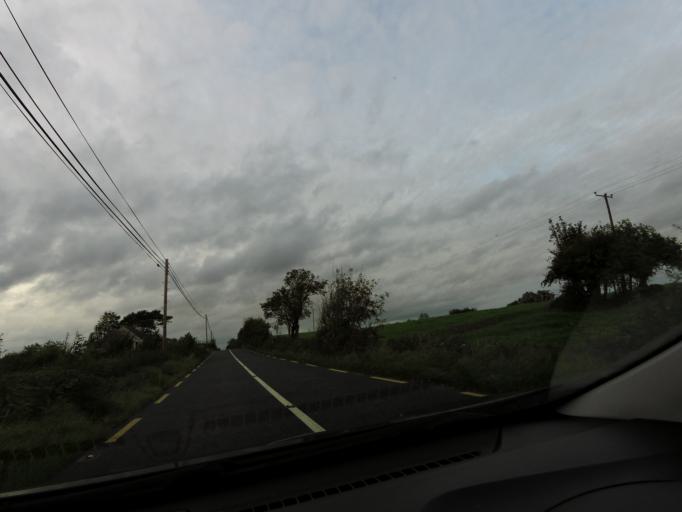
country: IE
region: Leinster
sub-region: An Iarmhi
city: Athlone
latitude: 53.3797
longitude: -7.8625
